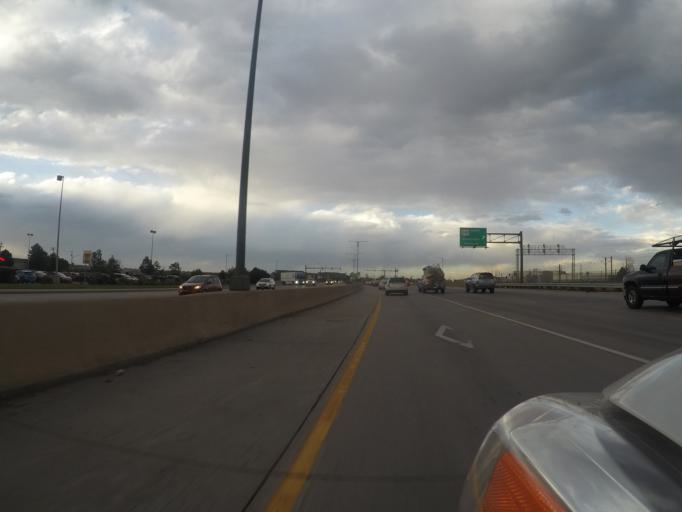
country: US
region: Colorado
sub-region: Arapahoe County
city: Englewood
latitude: 39.6505
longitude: -105.0028
